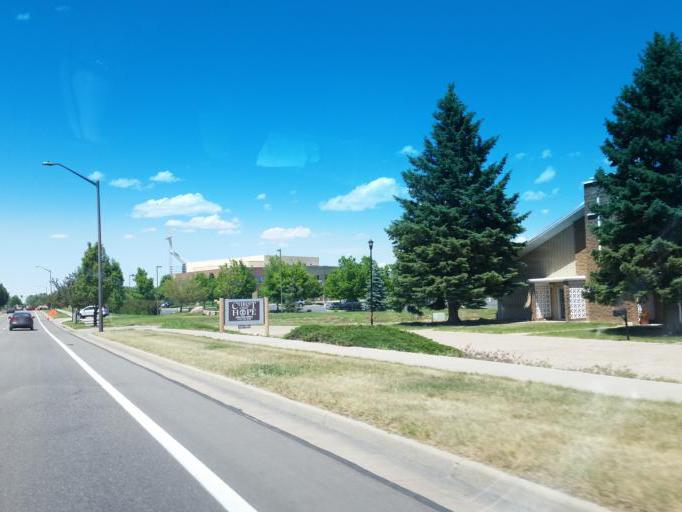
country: US
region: Colorado
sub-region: Larimer County
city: Fort Collins
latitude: 40.5311
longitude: -105.0961
